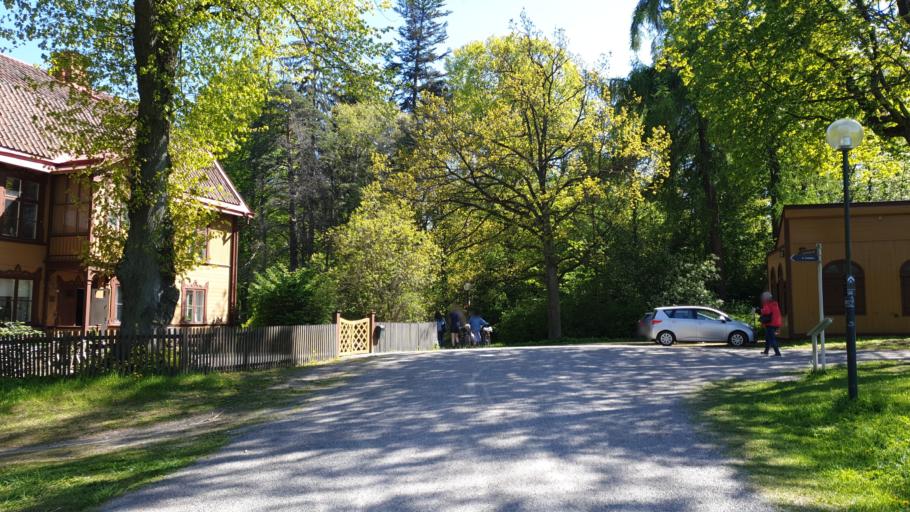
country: SE
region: Stockholm
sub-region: Norrtalje Kommun
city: Bergshamra
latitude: 59.3579
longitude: 18.0342
